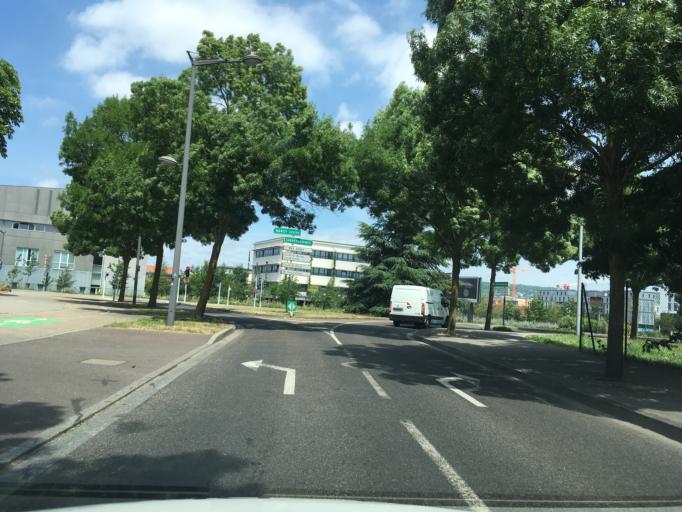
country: FR
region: Lorraine
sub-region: Departement de Meurthe-et-Moselle
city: Nancy
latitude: 48.6871
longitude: 6.1991
